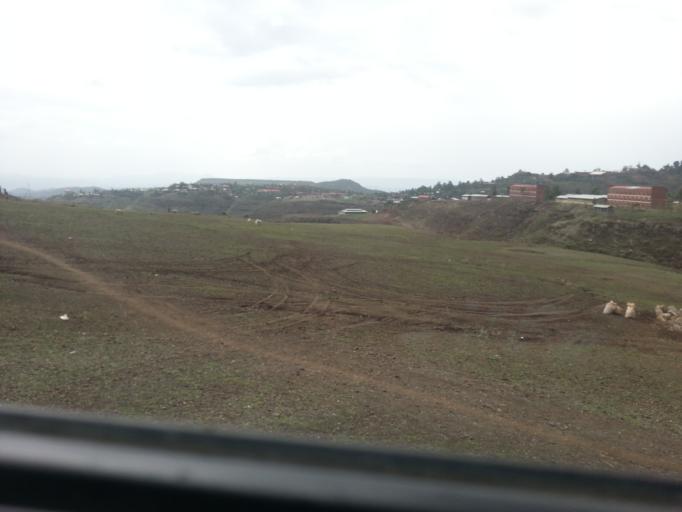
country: ET
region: Amhara
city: Lalibela
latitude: 12.0225
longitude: 39.0522
